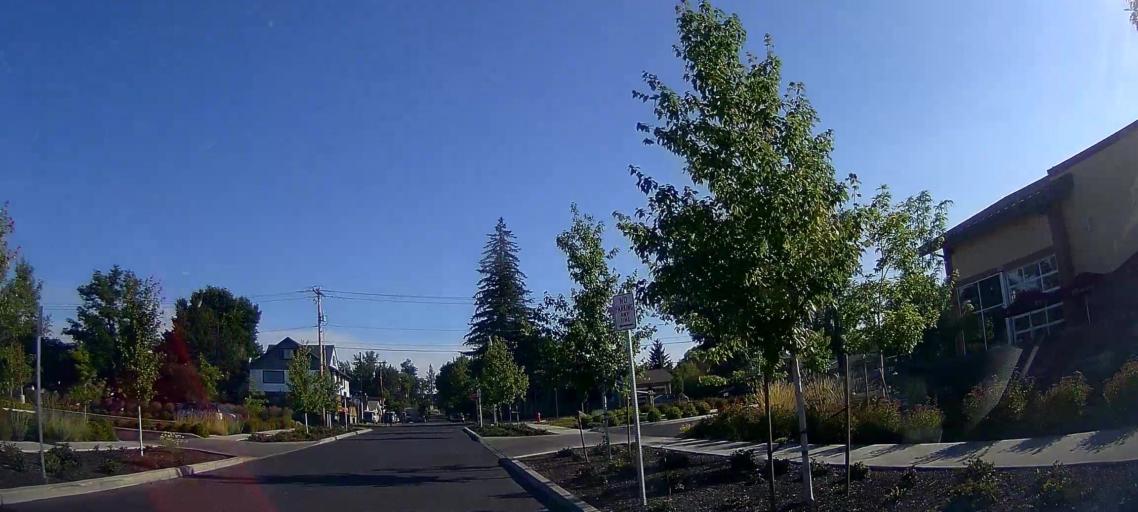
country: US
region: Oregon
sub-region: Deschutes County
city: Bend
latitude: 44.0539
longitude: -121.3112
